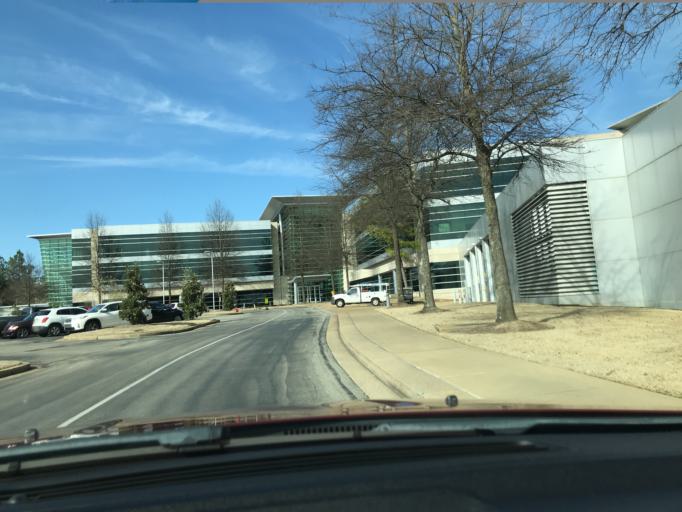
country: US
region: Tennessee
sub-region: Shelby County
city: Germantown
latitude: 35.0499
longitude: -89.7902
